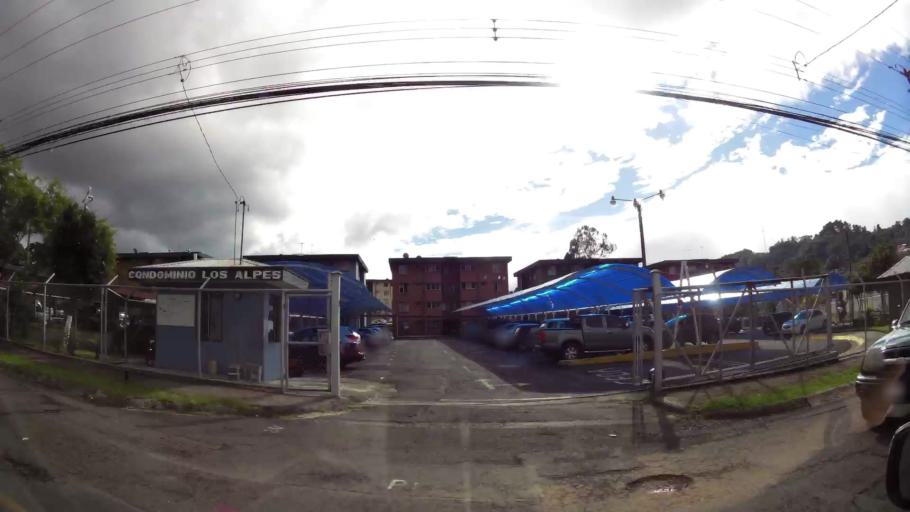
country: CR
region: San Jose
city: Curridabat
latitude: 9.9107
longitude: -84.0433
